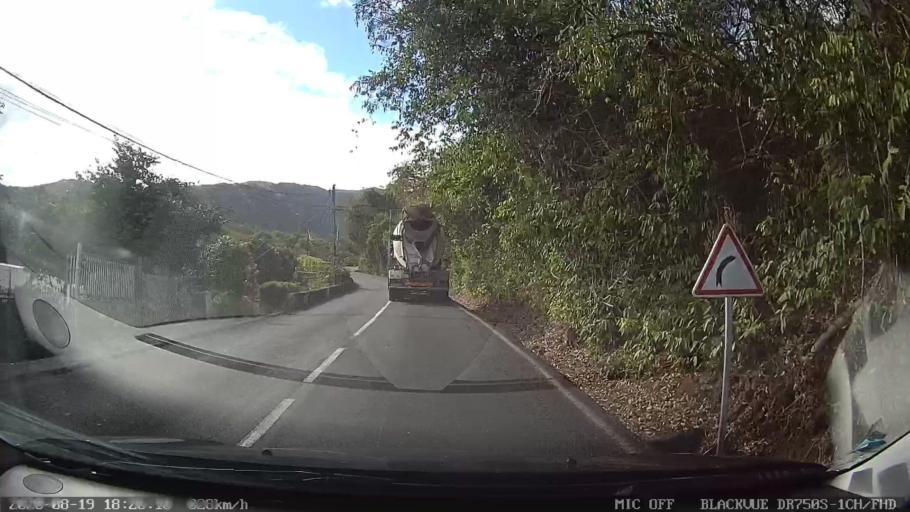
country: RE
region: Reunion
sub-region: Reunion
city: La Possession
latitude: -20.9543
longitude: 55.3510
